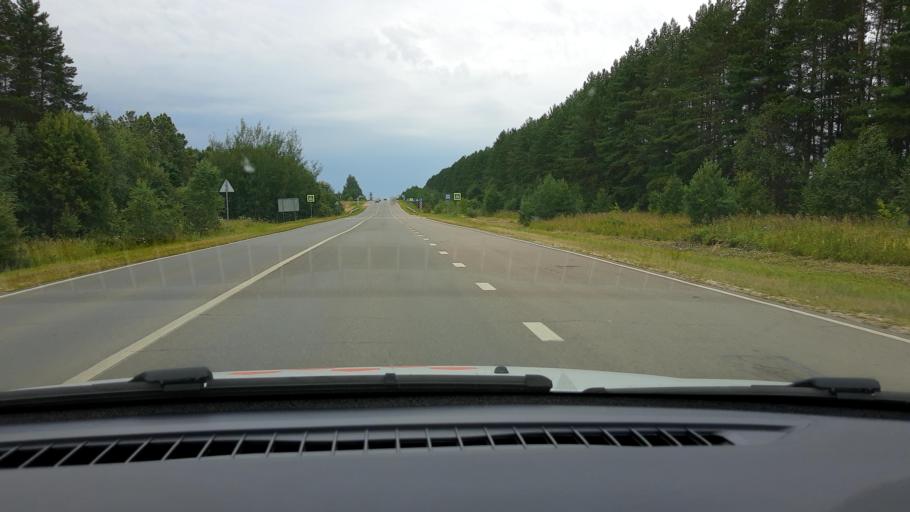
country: RU
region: Nizjnij Novgorod
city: Vyyezdnoye
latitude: 55.1540
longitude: 43.5736
